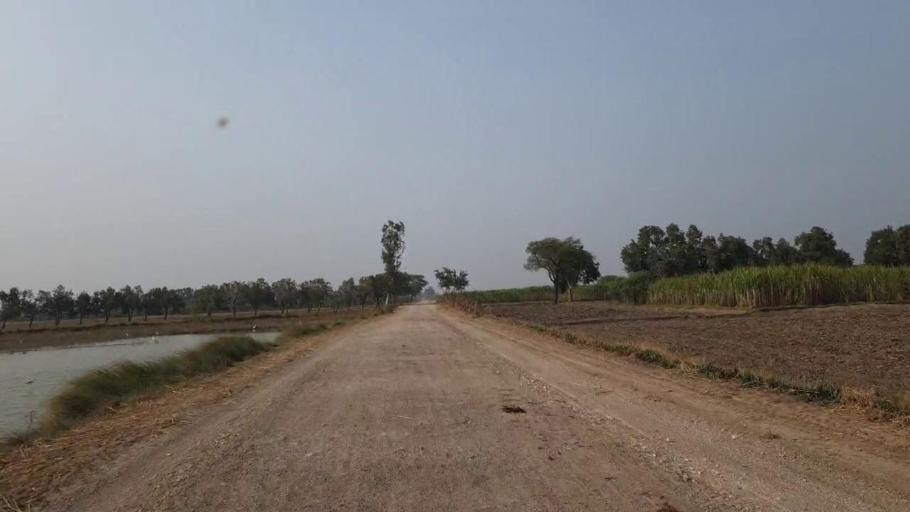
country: PK
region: Sindh
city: Matli
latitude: 25.0709
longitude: 68.5955
